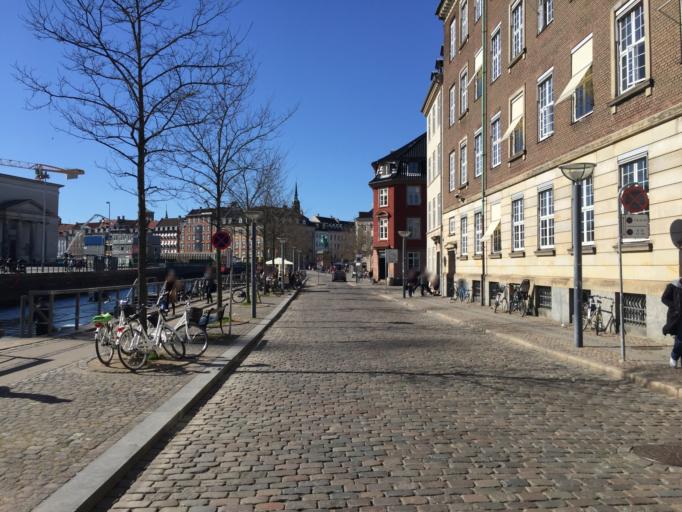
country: DK
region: Capital Region
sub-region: Kobenhavn
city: Christianshavn
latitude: 55.6769
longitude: 12.5823
